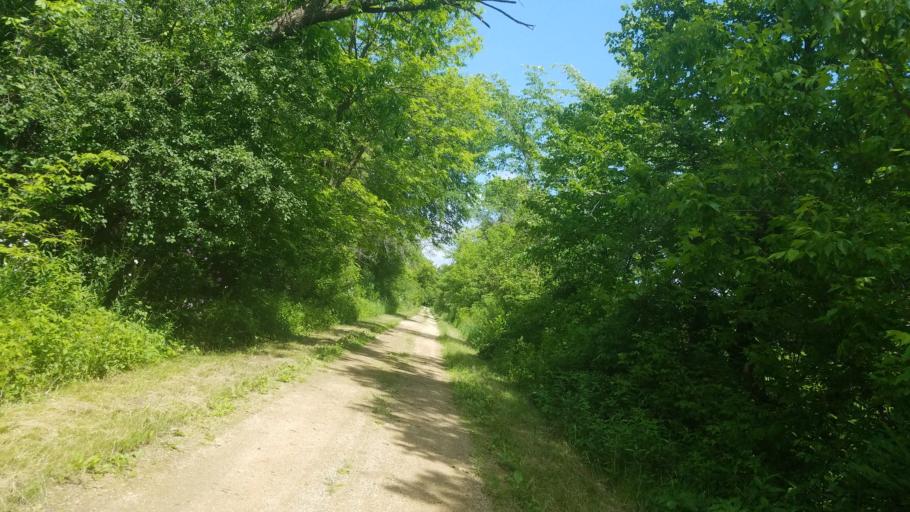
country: US
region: Wisconsin
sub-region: Dunn County
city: Menomonie
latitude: 44.7856
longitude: -91.9437
